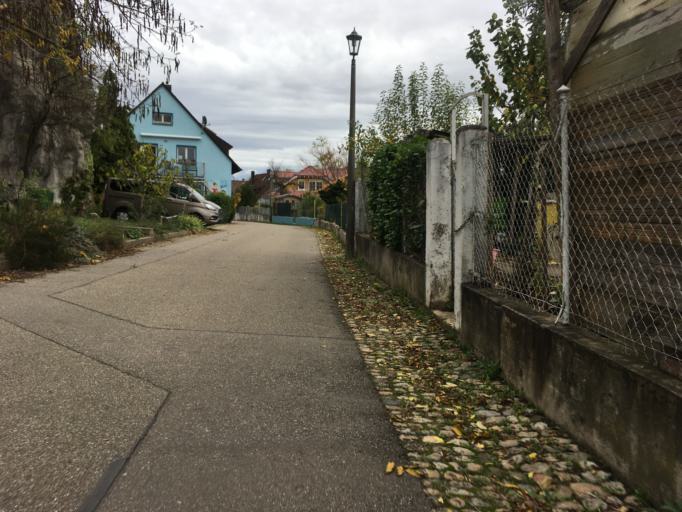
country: DE
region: Baden-Wuerttemberg
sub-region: Freiburg Region
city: Breisach am Rhein
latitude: 48.0286
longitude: 7.5790
